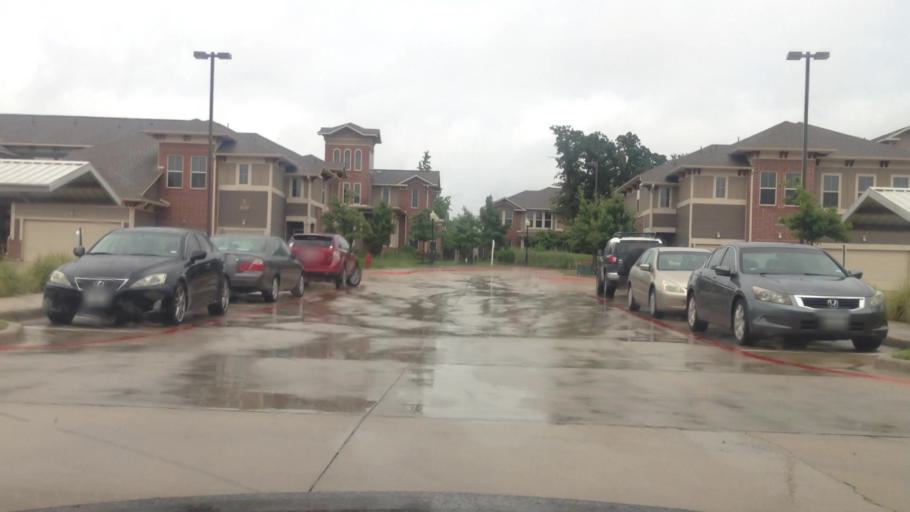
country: US
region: Texas
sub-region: Tarrant County
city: North Richland Hills
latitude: 32.8608
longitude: -97.1992
